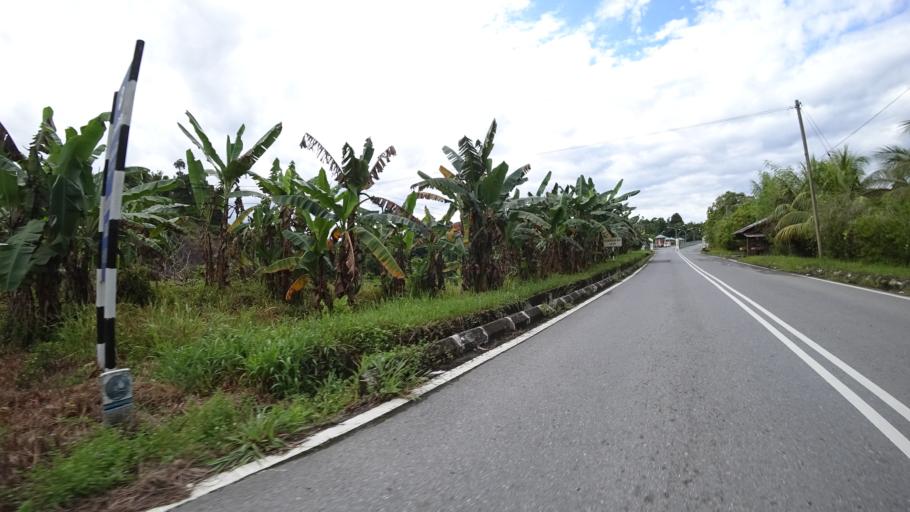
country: BN
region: Temburong
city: Bangar
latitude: 4.7909
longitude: 115.2377
